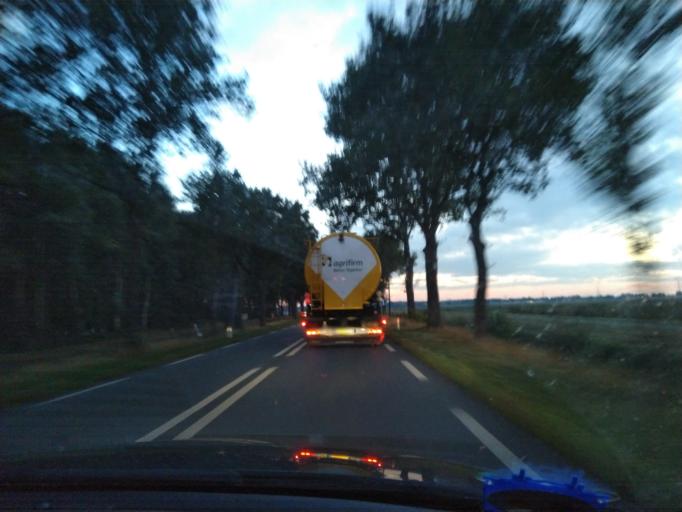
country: NL
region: Groningen
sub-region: Gemeente Pekela
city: Oude Pekela
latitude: 53.0974
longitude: 6.9816
